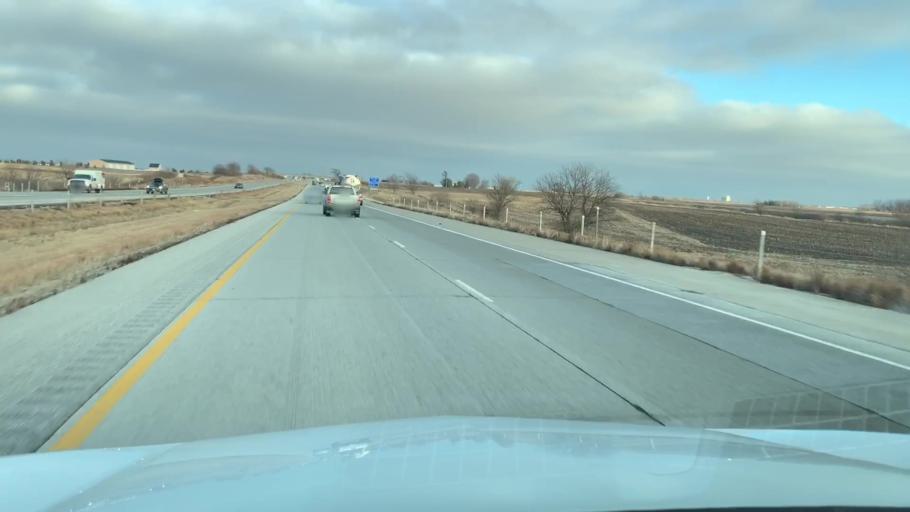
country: US
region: Iowa
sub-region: Polk County
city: Bondurant
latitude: 41.6771
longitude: -93.4171
